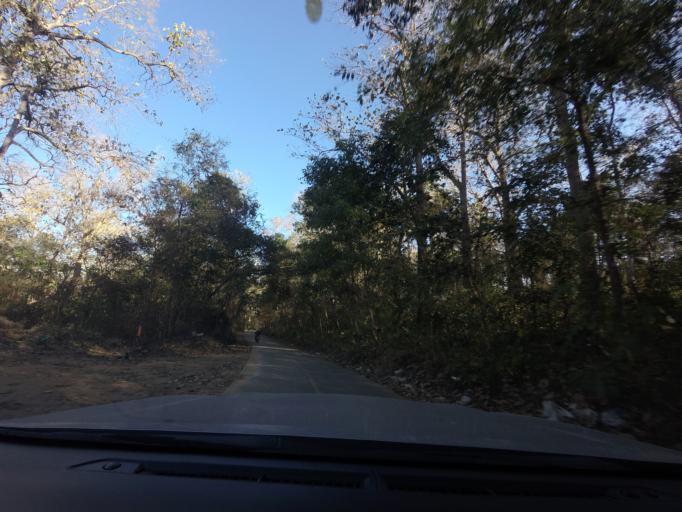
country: TH
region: Mae Hong Son
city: Wiang Nuea
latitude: 19.3995
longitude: 98.4194
